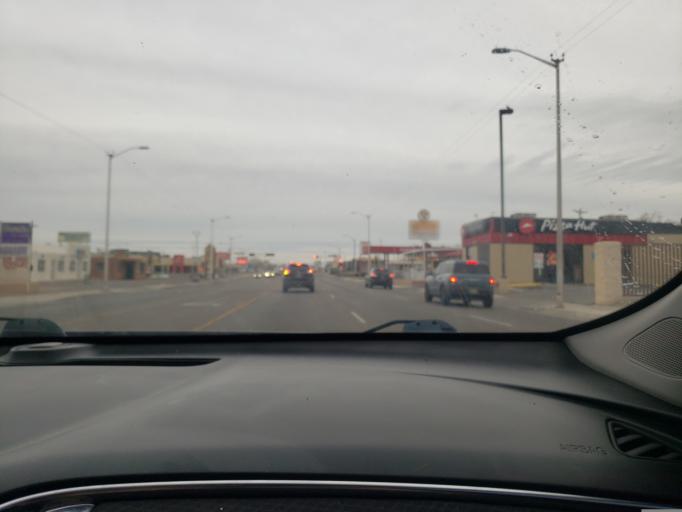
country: US
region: New Mexico
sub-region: Bernalillo County
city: North Valley
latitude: 35.1152
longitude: -106.5864
